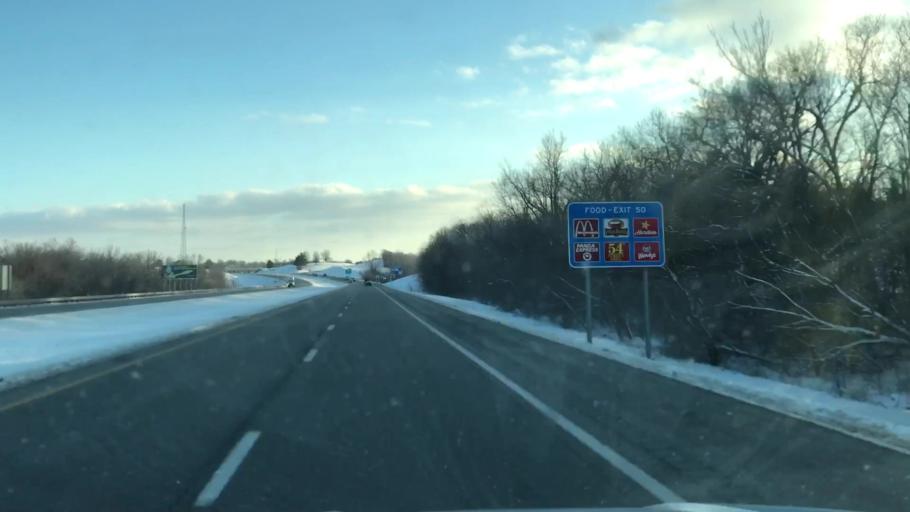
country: US
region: Missouri
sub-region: Andrew County
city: Country Club Village
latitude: 39.8249
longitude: -94.8055
